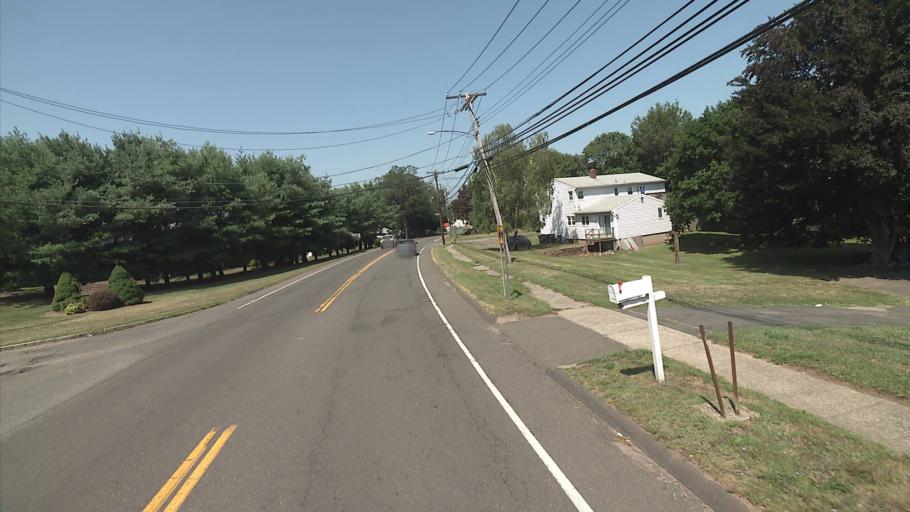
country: US
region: Connecticut
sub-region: New Haven County
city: East Haven
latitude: 41.2620
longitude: -72.8655
